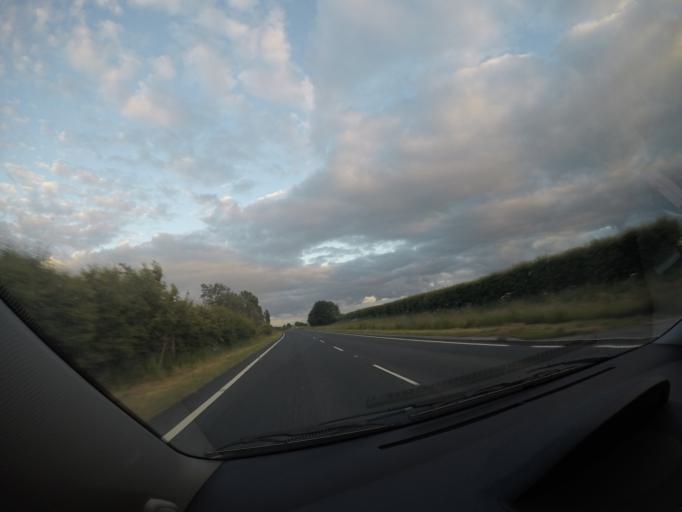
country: GB
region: England
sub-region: North Yorkshire
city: Bedale
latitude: 54.2507
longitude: -1.5084
